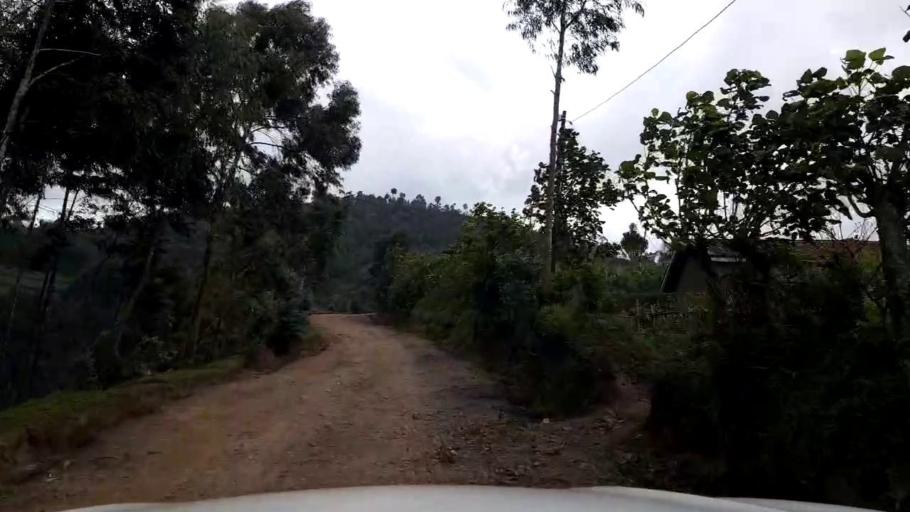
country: RW
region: Western Province
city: Kibuye
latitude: -1.9539
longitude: 29.4744
